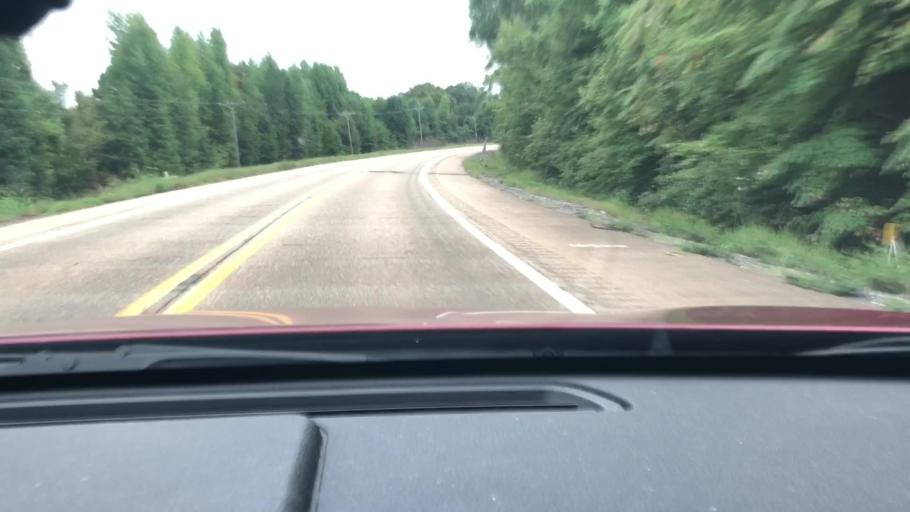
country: US
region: Arkansas
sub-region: Miller County
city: Texarkana
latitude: 33.4188
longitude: -93.8162
